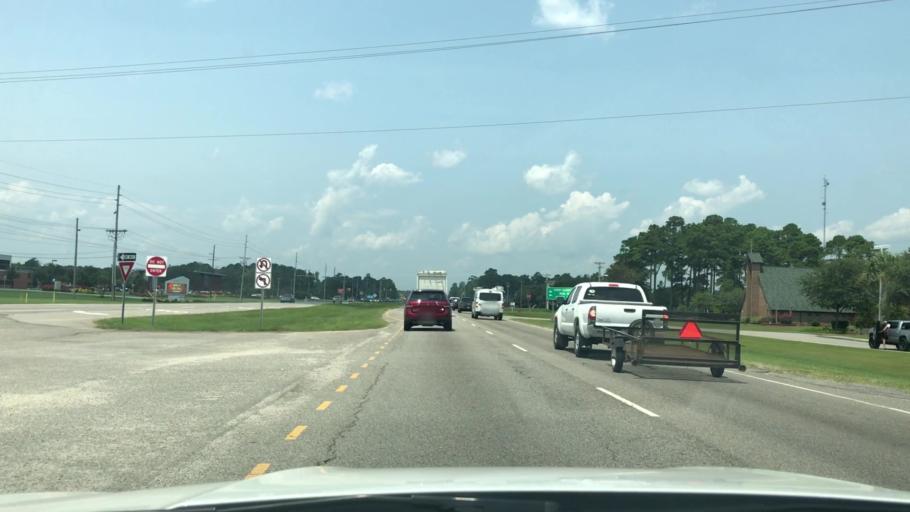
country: US
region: South Carolina
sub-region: Horry County
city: Red Hill
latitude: 33.7944
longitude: -79.0001
